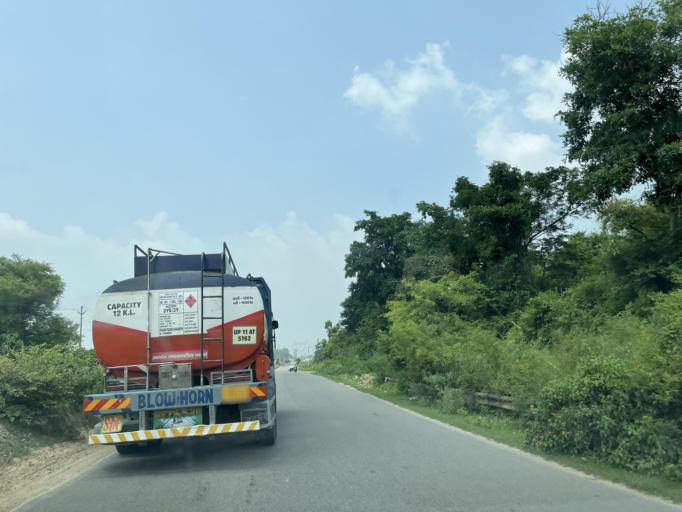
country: IN
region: Uttarakhand
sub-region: Haridwar
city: Haridwar
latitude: 29.8576
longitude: 78.1861
